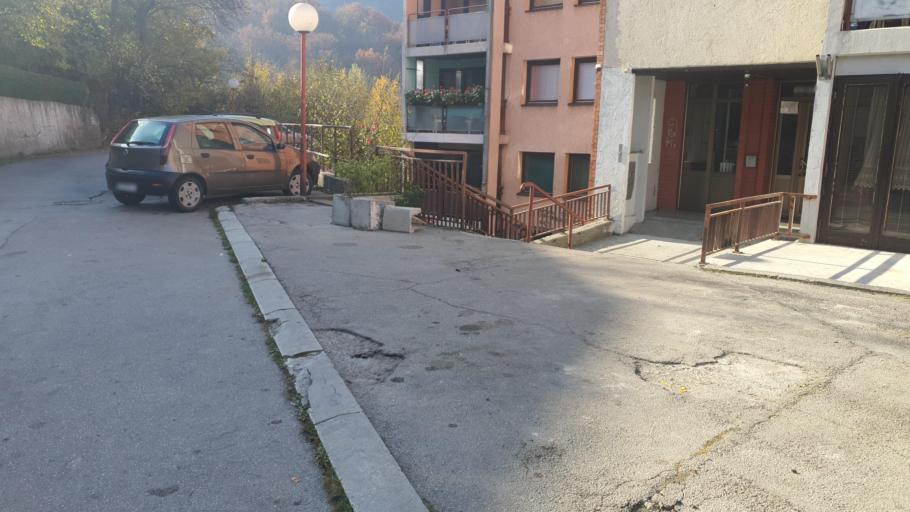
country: RS
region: Central Serbia
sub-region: Zlatiborski Okrug
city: Uzice
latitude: 43.8471
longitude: 19.8657
